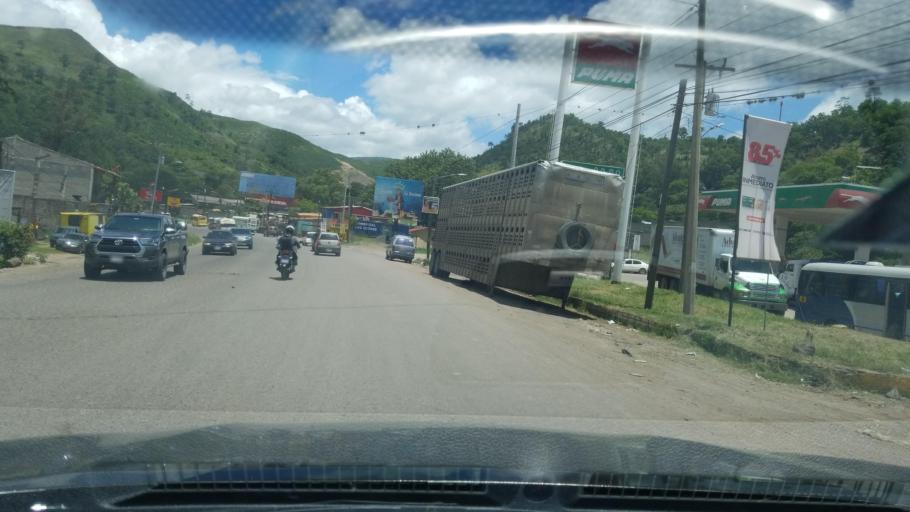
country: HN
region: Francisco Morazan
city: Rio Abajo
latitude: 14.1380
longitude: -87.2330
